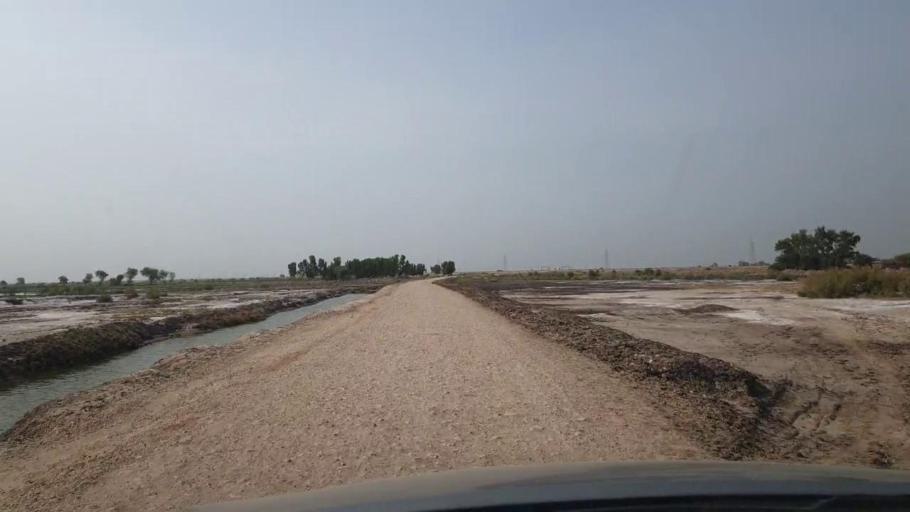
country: PK
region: Sindh
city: Lakhi
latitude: 27.8364
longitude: 68.6998
